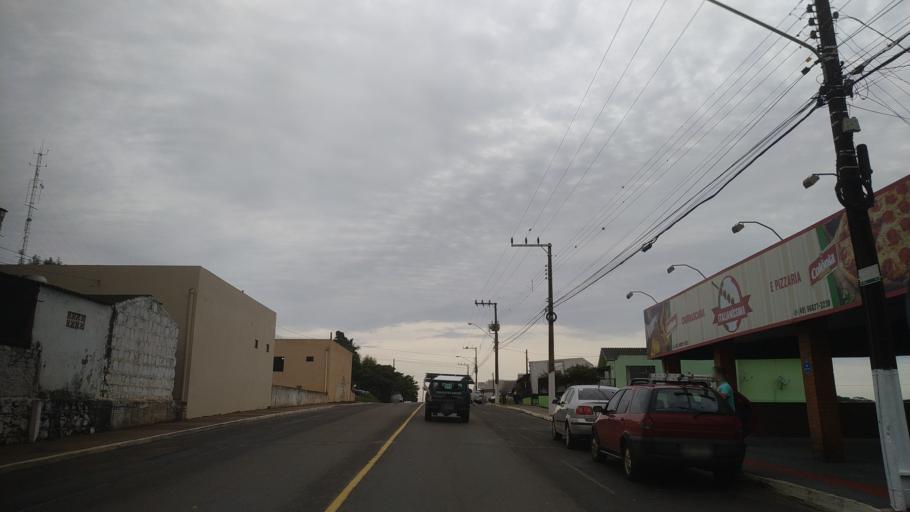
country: BR
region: Santa Catarina
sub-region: Chapeco
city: Chapeco
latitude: -27.0984
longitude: -52.6738
